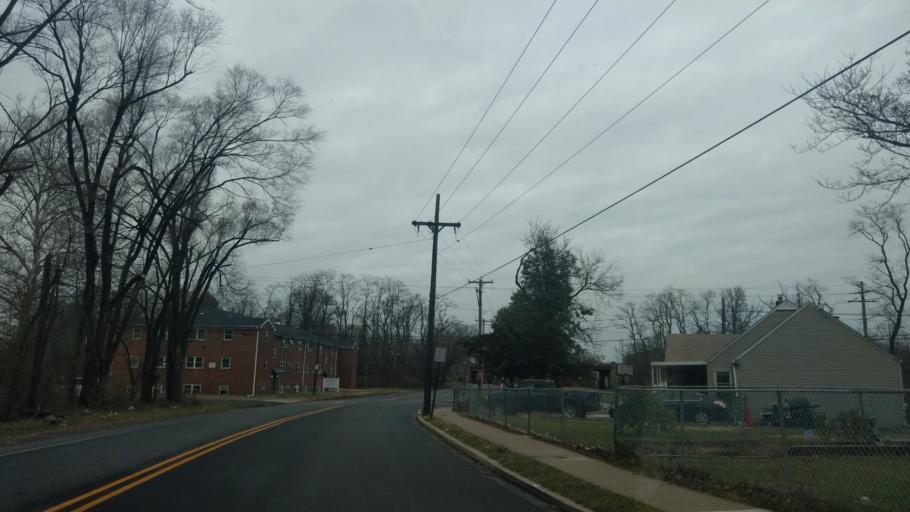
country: US
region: Pennsylvania
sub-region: Bucks County
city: Bristol
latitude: 40.1201
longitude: -74.8479
